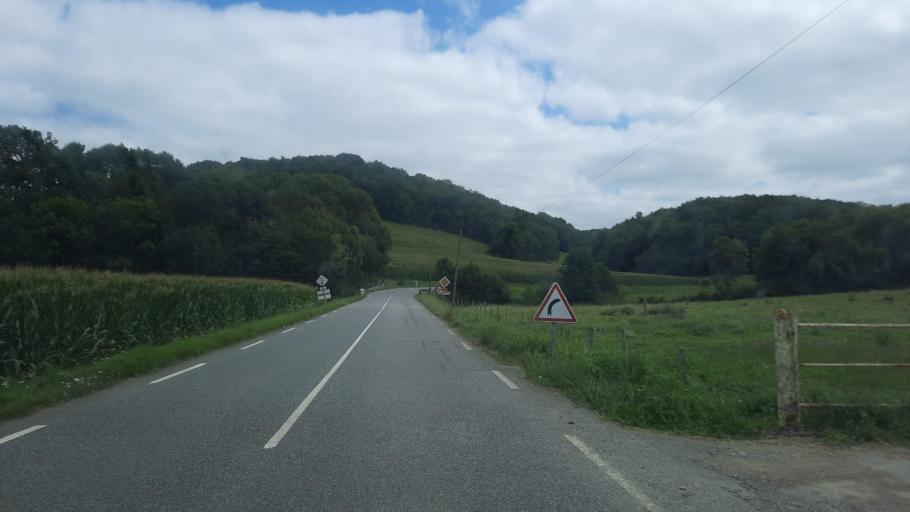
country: FR
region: Midi-Pyrenees
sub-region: Departement des Hautes-Pyrenees
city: Trie-sur-Baise
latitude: 43.3049
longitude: 0.2680
